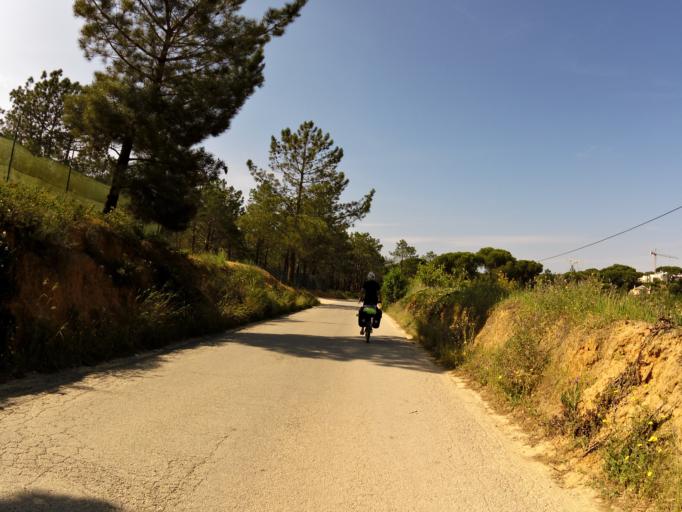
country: PT
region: Faro
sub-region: Loule
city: Almancil
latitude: 37.0609
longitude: -8.0160
